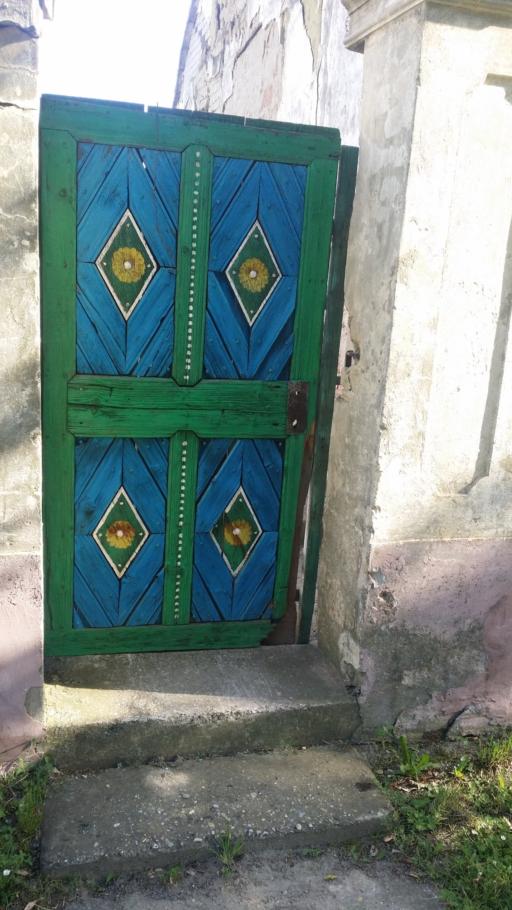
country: HU
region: Baranya
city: Vajszlo
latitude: 45.8665
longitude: 18.0816
